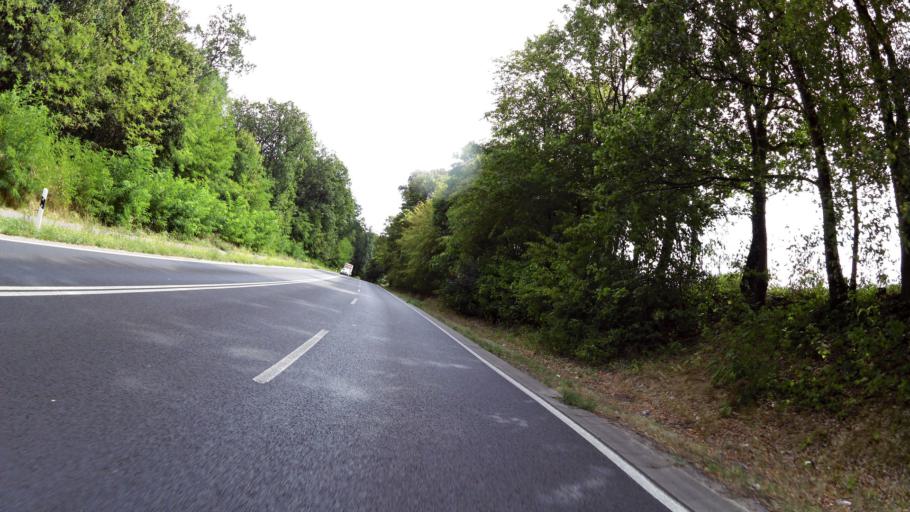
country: DE
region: Brandenburg
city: Neuzelle
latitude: 52.0823
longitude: 14.6562
